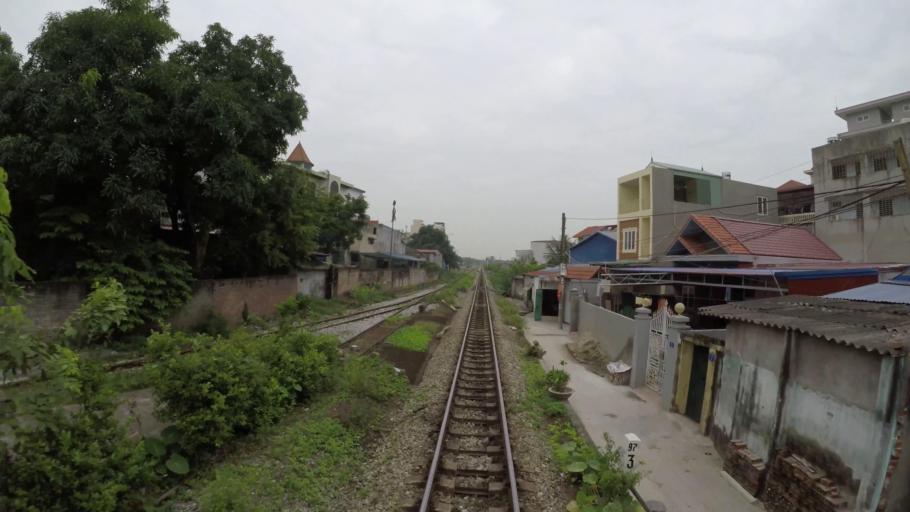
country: VN
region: Hai Phong
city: An Duong
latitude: 20.8847
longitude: 106.6036
